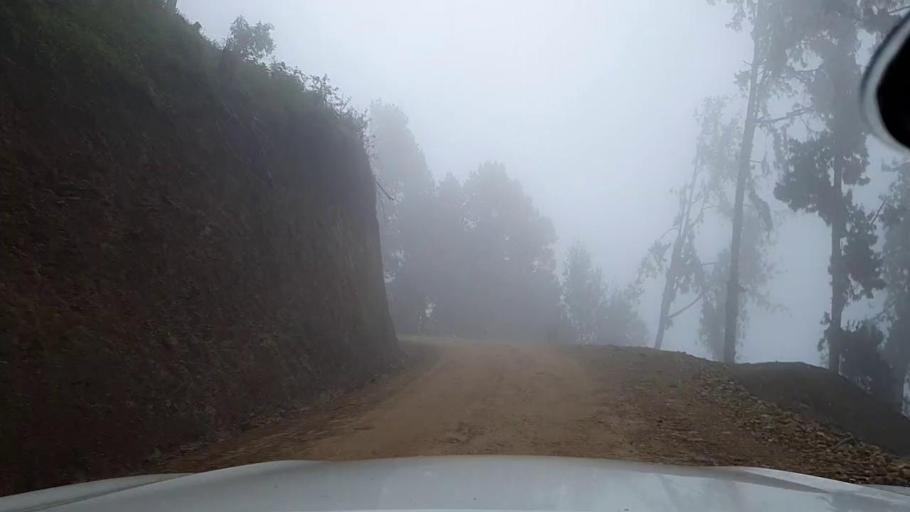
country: BI
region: Cibitoke
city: Cibitoke
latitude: -2.5991
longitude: 29.1954
